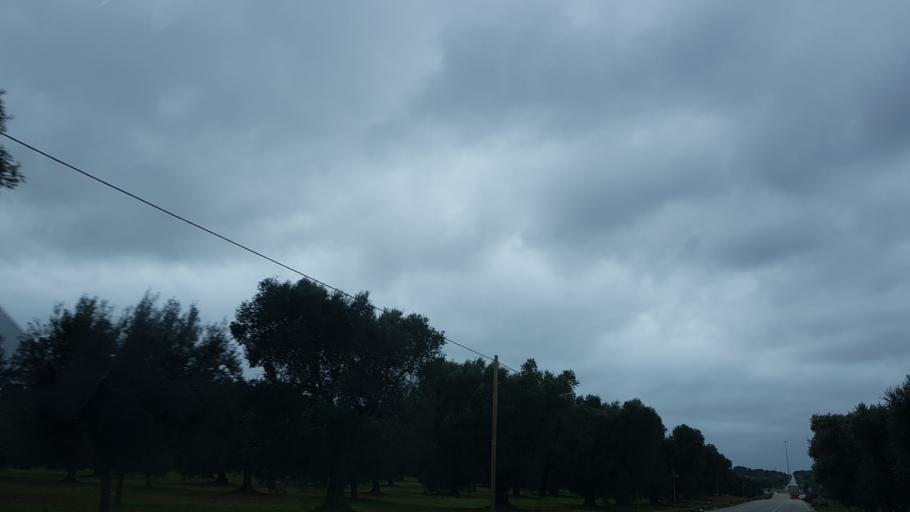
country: IT
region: Apulia
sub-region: Provincia di Brindisi
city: San Vito dei Normanni
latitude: 40.6537
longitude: 17.7811
